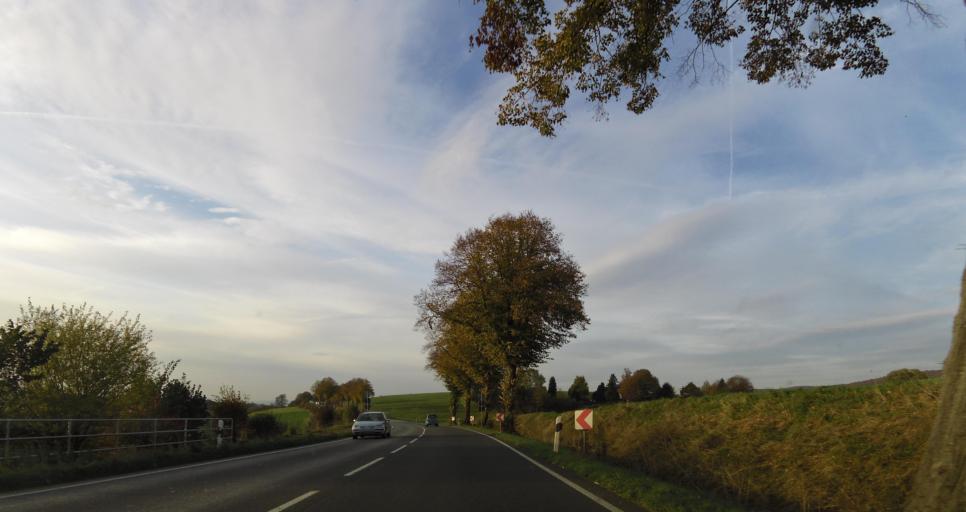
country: DE
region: Lower Saxony
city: Kreiensen
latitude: 51.7751
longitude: 9.9428
